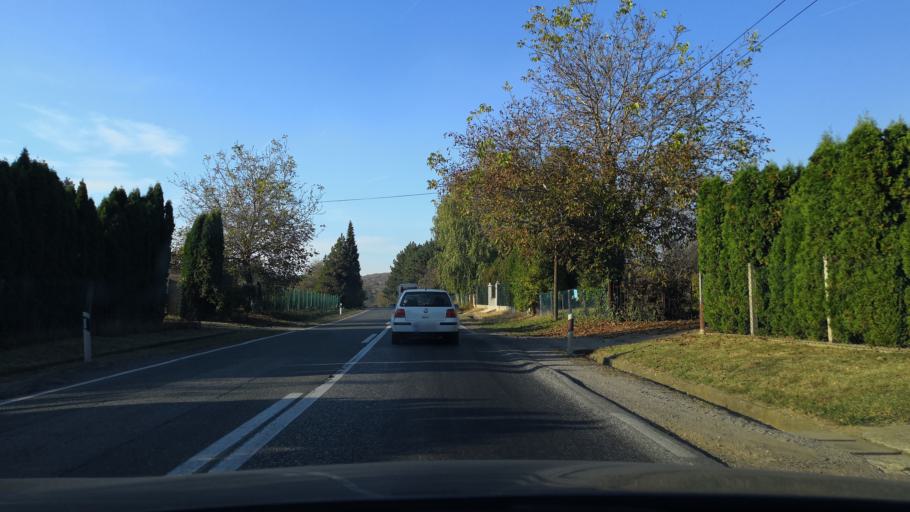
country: RS
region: Autonomna Pokrajina Vojvodina
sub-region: Sremski Okrug
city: Irig
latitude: 45.1296
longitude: 19.8420
